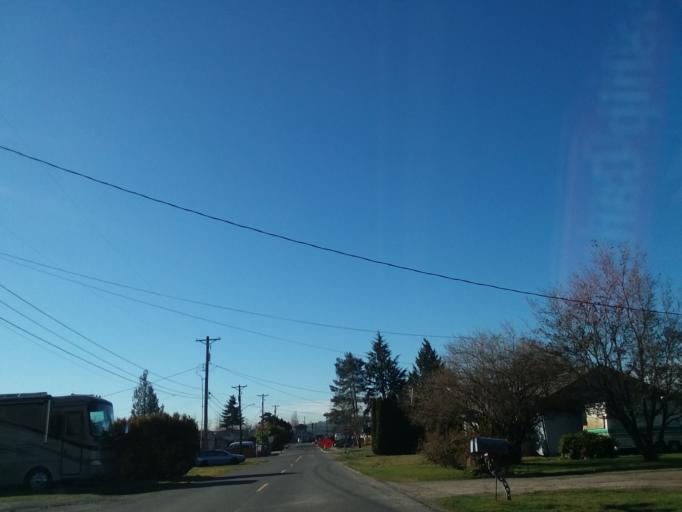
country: US
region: Washington
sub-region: Pierce County
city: Fife
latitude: 47.2452
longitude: -122.3662
